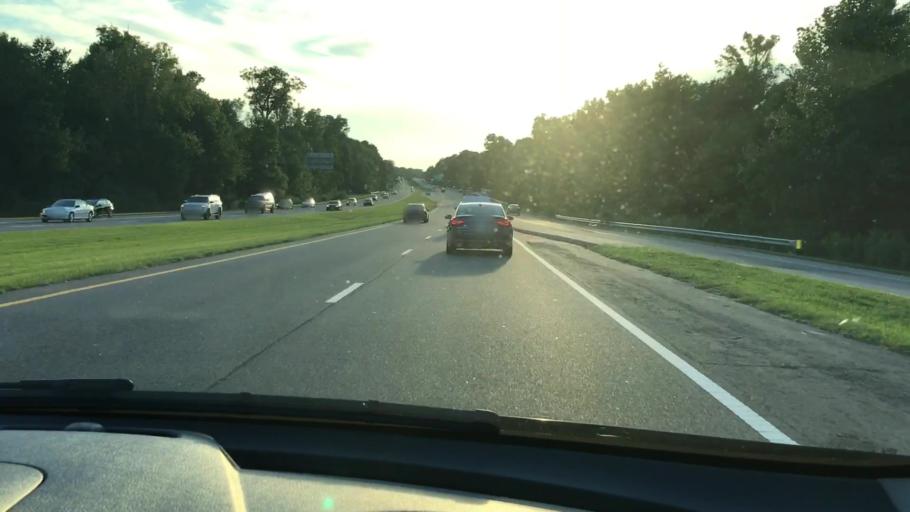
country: US
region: Virginia
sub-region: City of Hampton
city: Hampton
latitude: 37.0604
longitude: -76.4043
